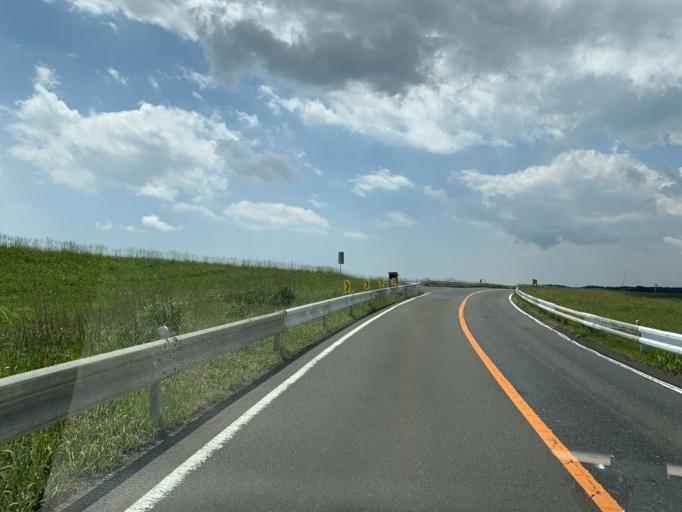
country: JP
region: Miyagi
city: Matsushima
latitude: 38.4428
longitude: 141.0801
